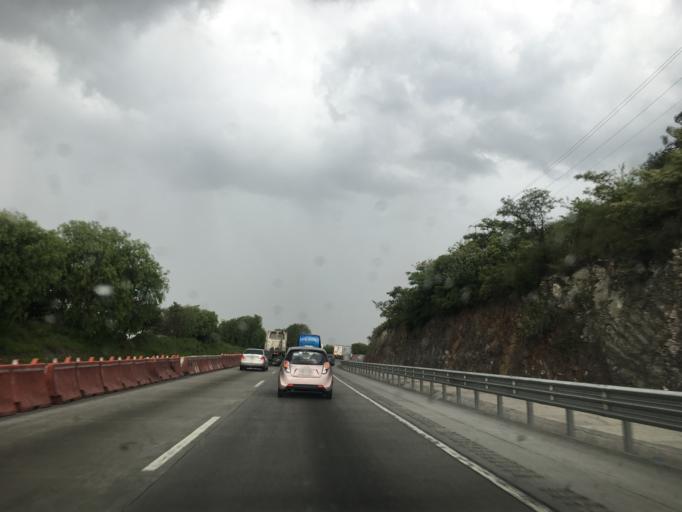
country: MX
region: Hidalgo
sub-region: Tepeji del Rio de Ocampo
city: Cantera de Villagran
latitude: 19.8613
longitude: -99.3176
